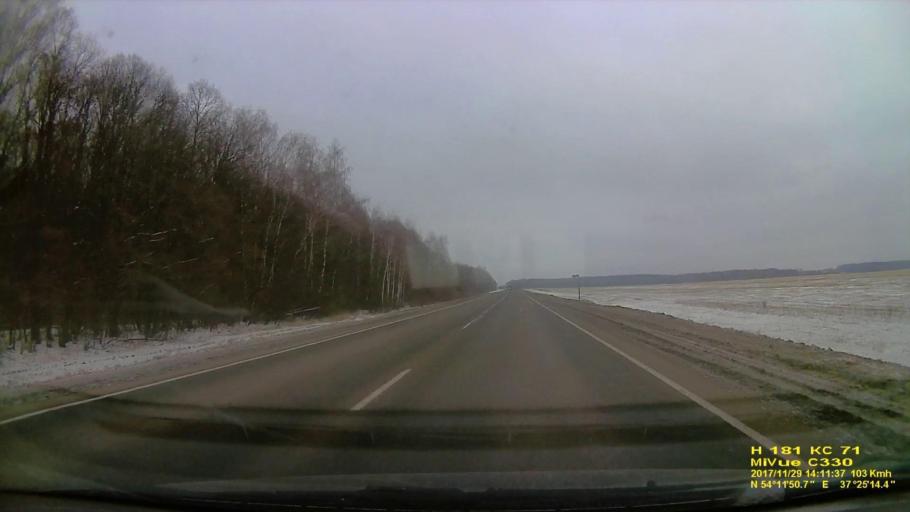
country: RU
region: Tula
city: Barsuki
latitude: 54.1972
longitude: 37.4209
